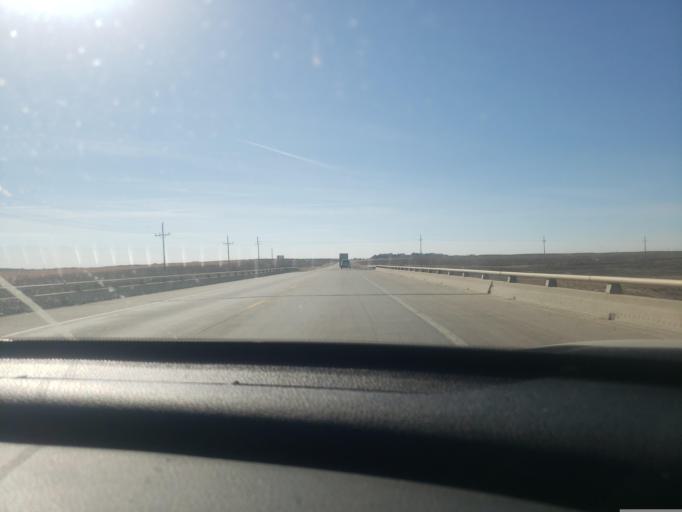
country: US
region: Kansas
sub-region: Finney County
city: Garden City
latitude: 37.9487
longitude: -100.8443
